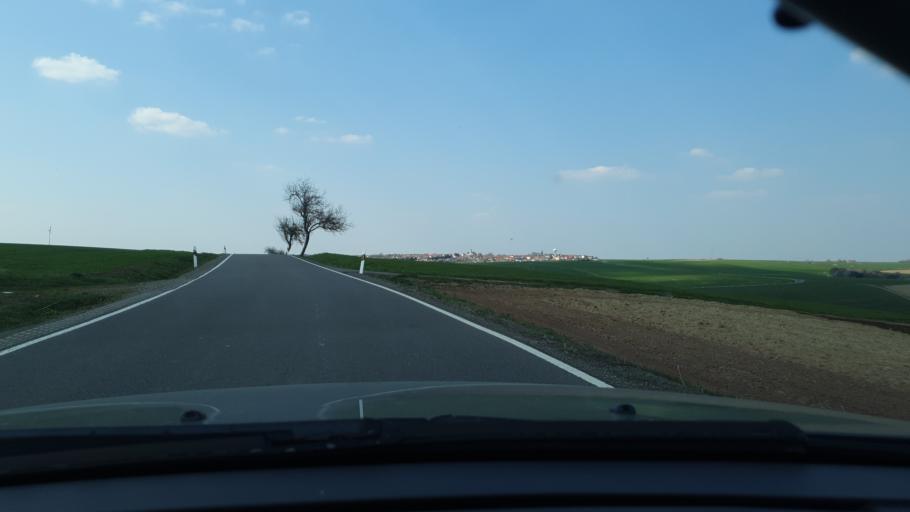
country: DE
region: Rheinland-Pfalz
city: Knopp-Labach
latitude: 49.3421
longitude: 7.4884
